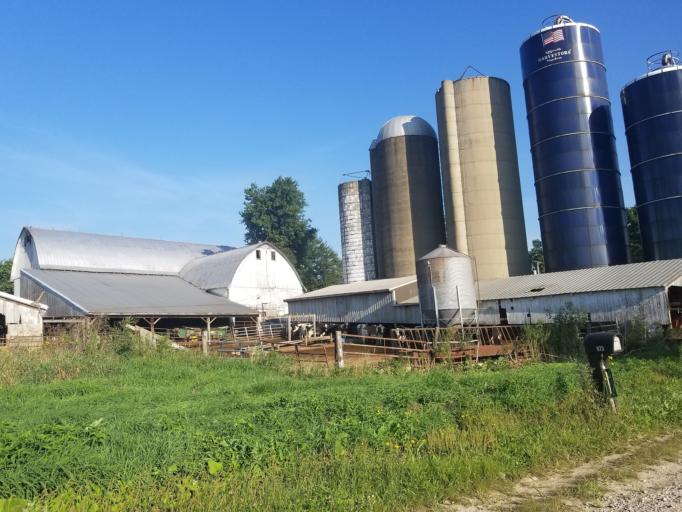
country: US
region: Ohio
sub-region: Ashland County
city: Ashland
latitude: 40.9348
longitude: -82.3686
